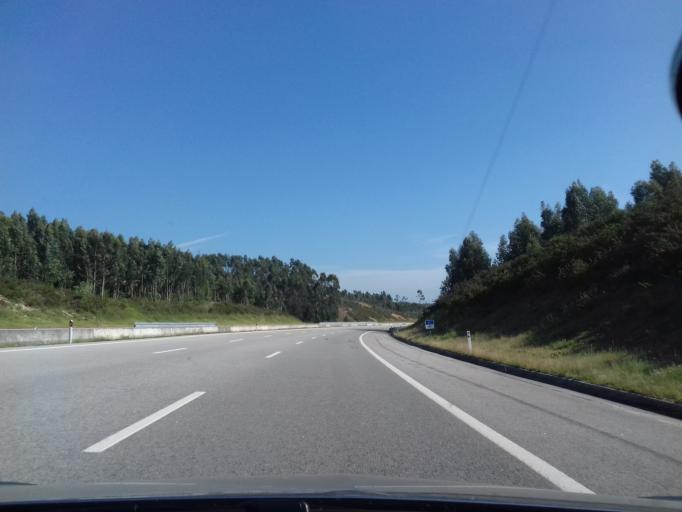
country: PT
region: Coimbra
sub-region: Figueira da Foz
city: Alhadas
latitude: 40.1346
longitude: -8.7446
